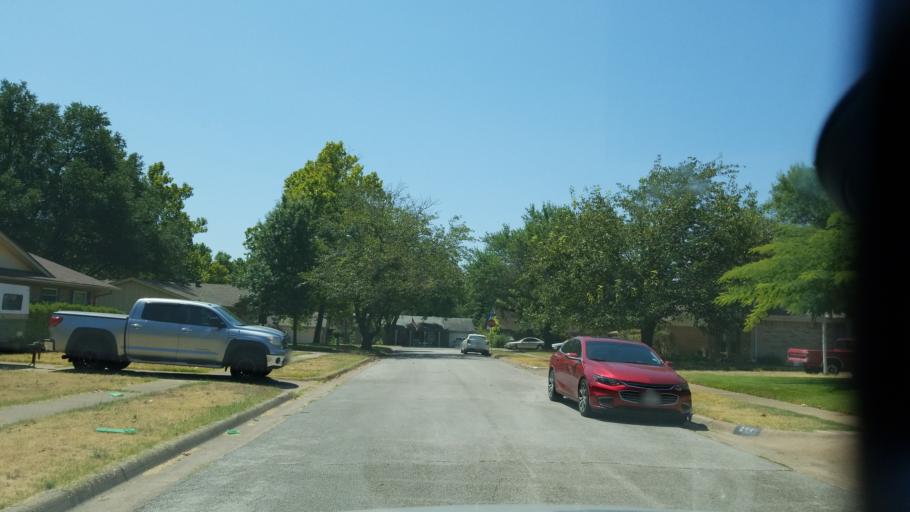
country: US
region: Texas
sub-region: Dallas County
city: Duncanville
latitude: 32.6532
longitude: -96.9043
